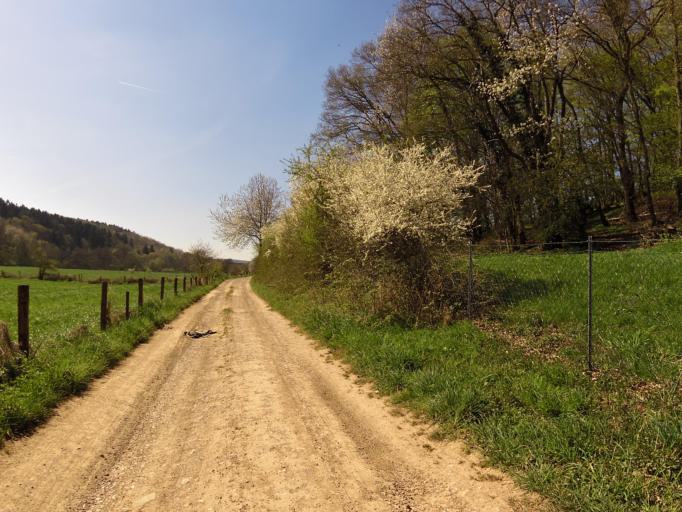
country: DE
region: North Rhine-Westphalia
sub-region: Regierungsbezirk Koln
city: Euskirchen
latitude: 50.5981
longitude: 6.8453
